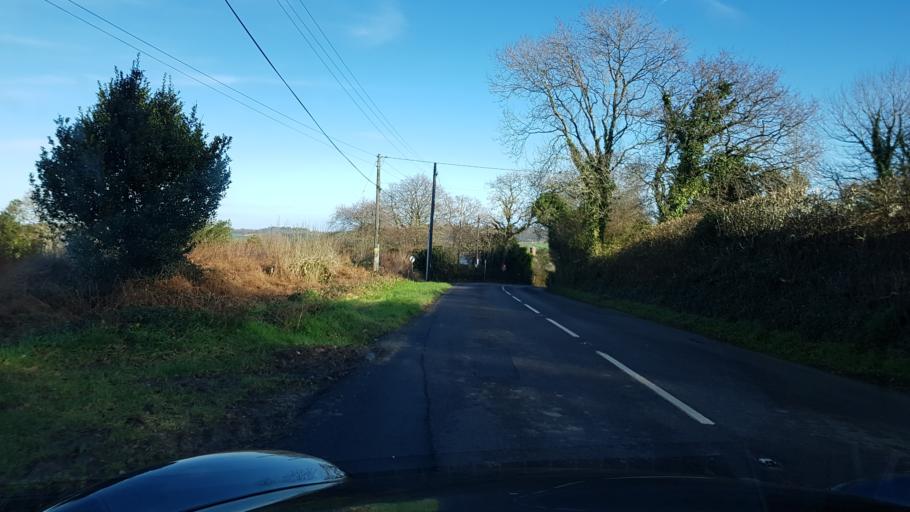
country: GB
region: England
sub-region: Dorset
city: Lyme Regis
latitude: 50.7926
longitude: -2.8868
